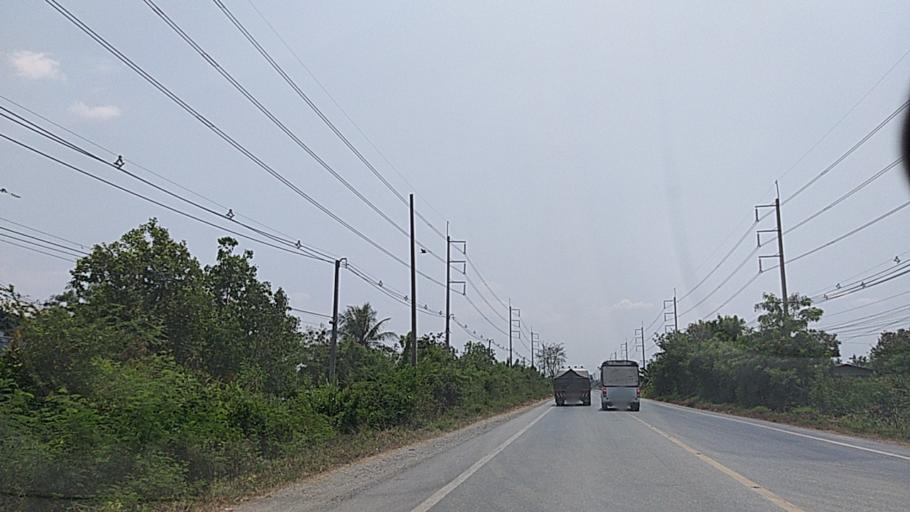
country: TH
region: Chachoengsao
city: Bang Nam Priao
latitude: 13.8419
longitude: 101.0526
